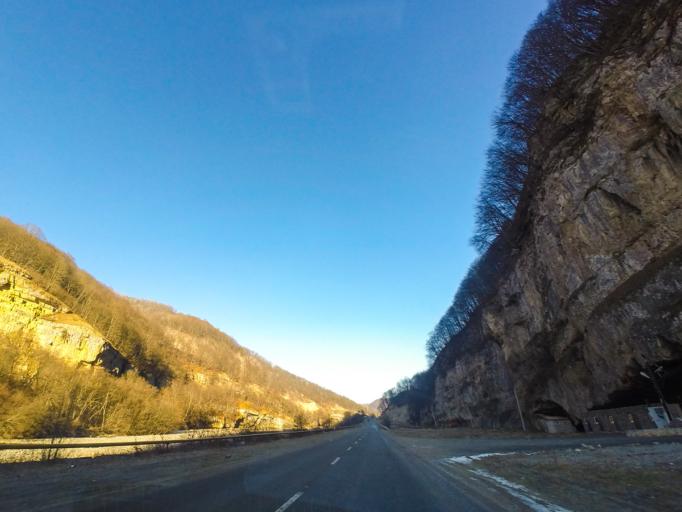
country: RU
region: Kabardino-Balkariya
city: Zhankhoteko
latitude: 43.4691
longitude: 43.2634
